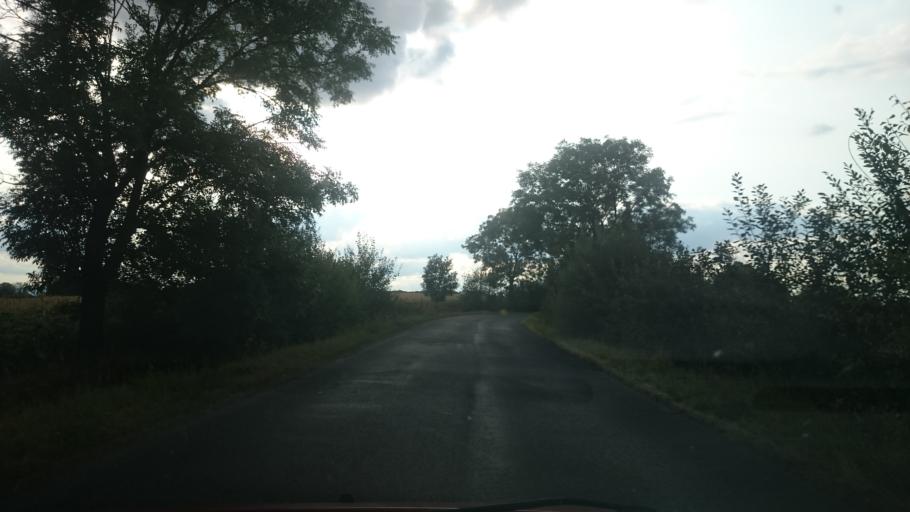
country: PL
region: Opole Voivodeship
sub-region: Powiat nyski
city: Otmuchow
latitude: 50.5003
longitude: 17.2050
